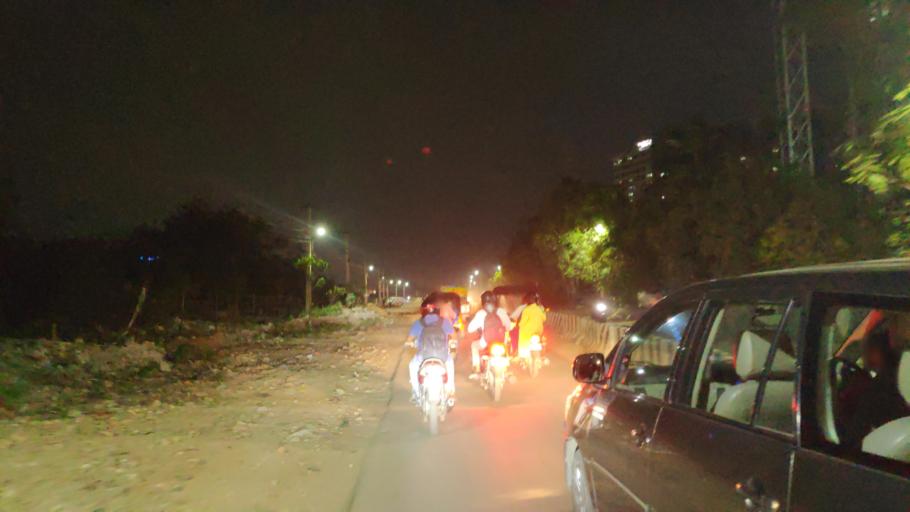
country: IN
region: Telangana
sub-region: Rangareddi
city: Kukatpalli
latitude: 17.4758
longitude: 78.3805
